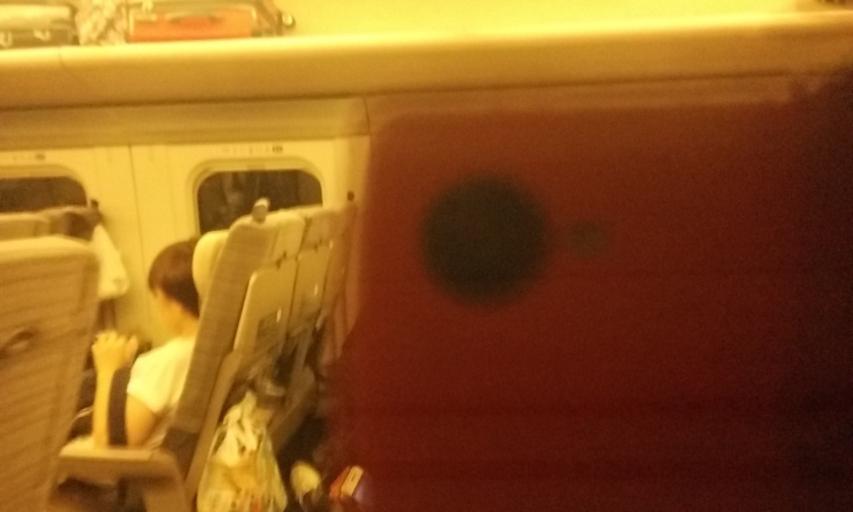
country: JP
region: Tochigi
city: Yaita
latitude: 36.7939
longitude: 139.9547
